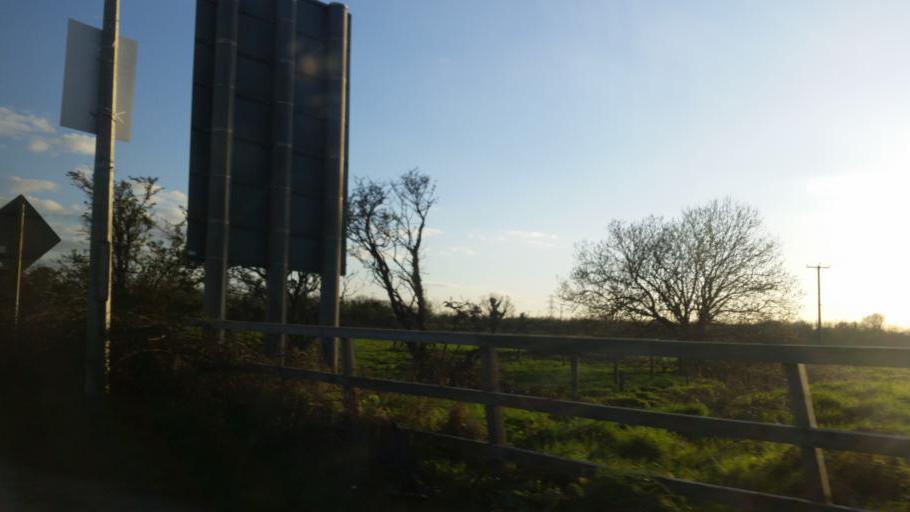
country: IE
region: Leinster
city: Lusk
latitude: 53.5000
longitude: -6.1941
